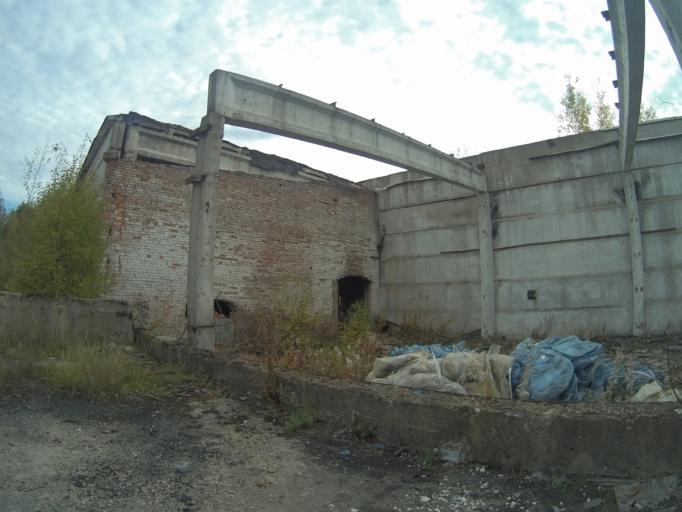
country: RU
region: Vladimir
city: Golovino
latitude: 55.9688
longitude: 40.4183
